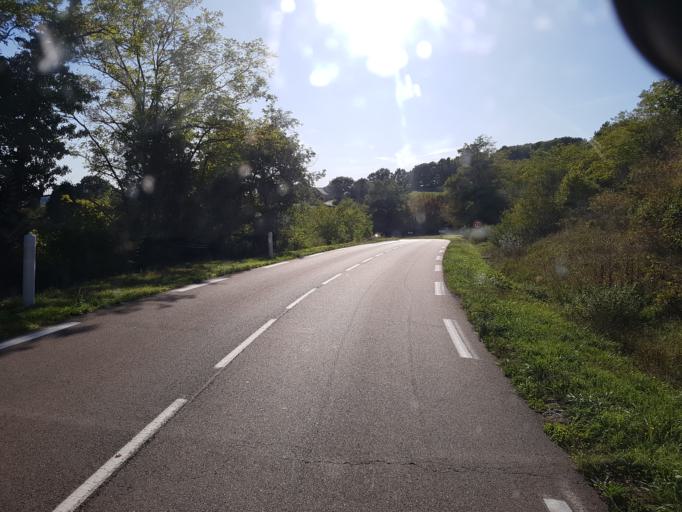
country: FR
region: Bourgogne
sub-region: Departement de Saone-et-Loire
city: Autun
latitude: 47.0455
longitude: 4.2762
